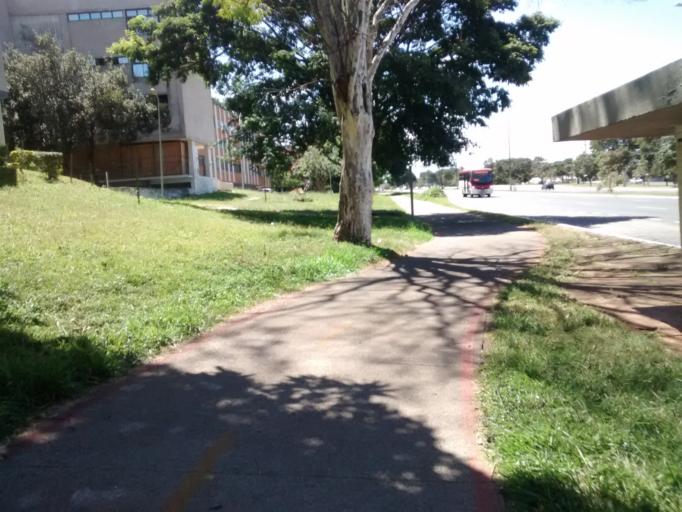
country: BR
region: Federal District
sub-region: Brasilia
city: Brasilia
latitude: -15.8186
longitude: -47.8927
